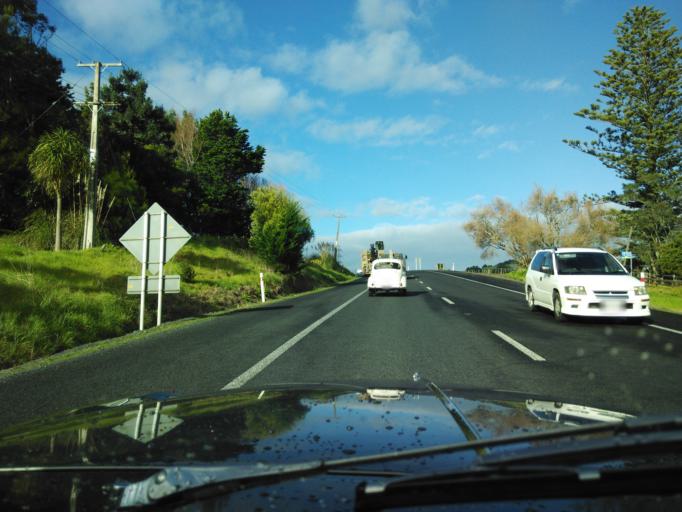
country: NZ
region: Auckland
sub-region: Auckland
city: Wellsford
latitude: -36.1755
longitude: 174.4494
